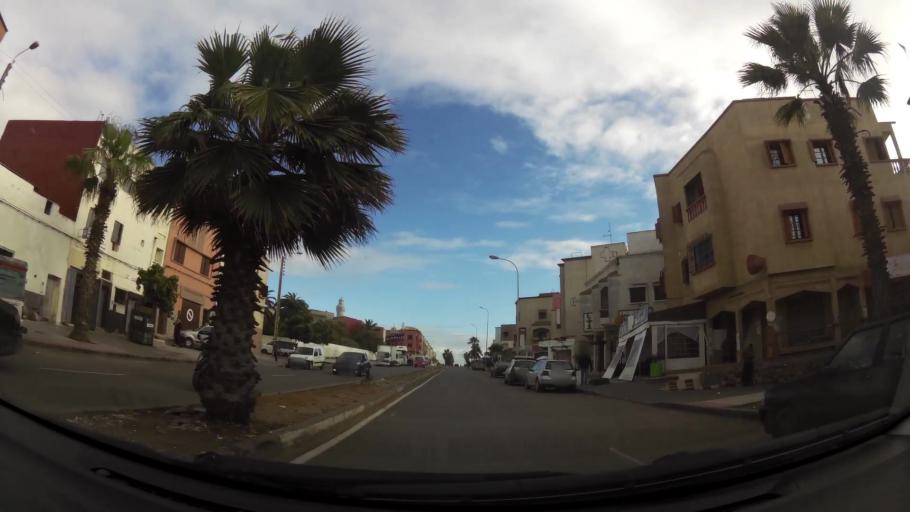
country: MA
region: Doukkala-Abda
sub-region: El-Jadida
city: El Jadida
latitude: 33.2533
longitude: -8.5183
